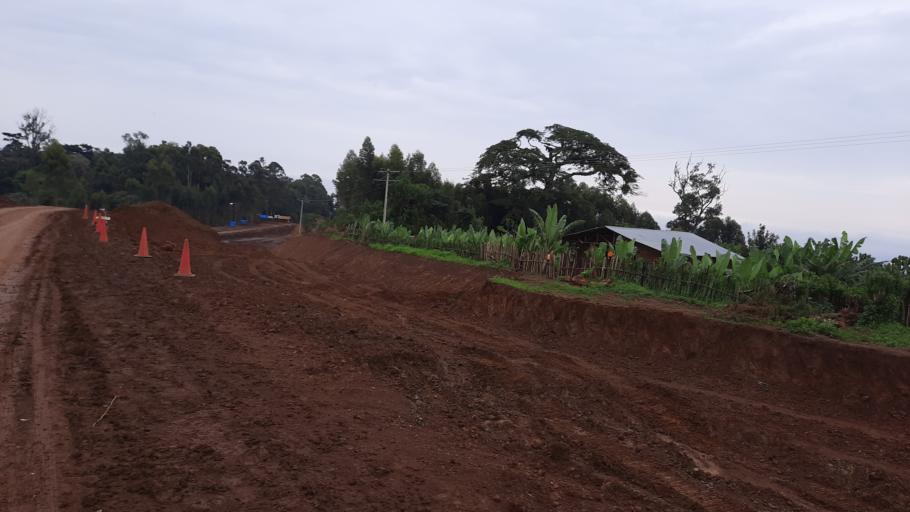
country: ET
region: Oromiya
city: Gore
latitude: 7.8139
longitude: 35.4586
